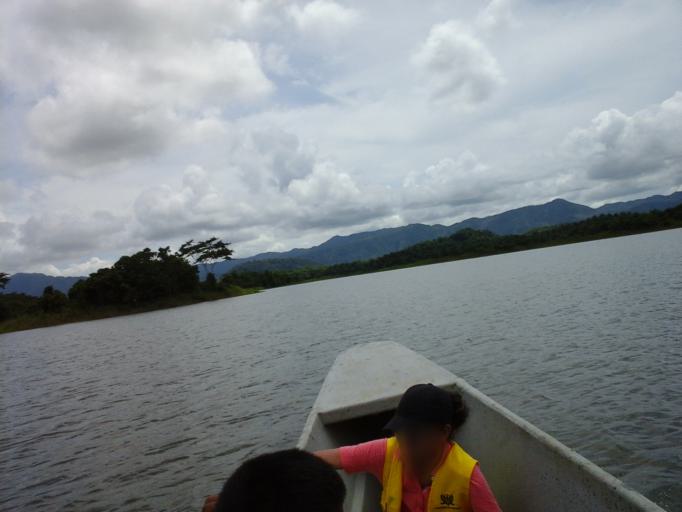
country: CO
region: Bolivar
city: San Cristobal
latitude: 9.8720
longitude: -75.2944
